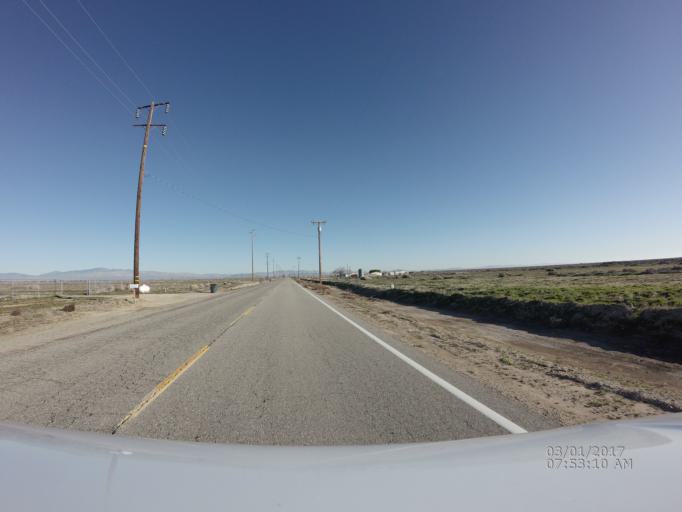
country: US
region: California
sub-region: Los Angeles County
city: Quartz Hill
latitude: 34.7372
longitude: -118.2548
